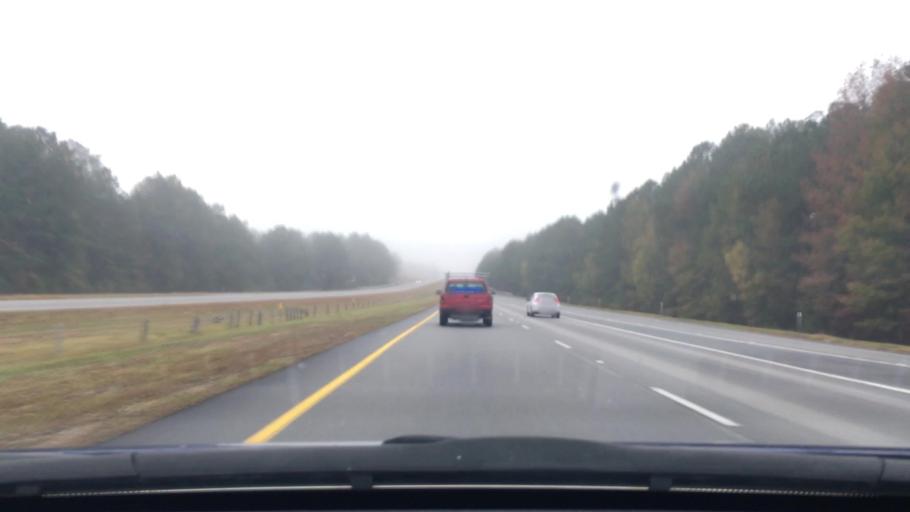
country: US
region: South Carolina
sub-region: Lee County
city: Bishopville
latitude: 34.2126
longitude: -80.4252
